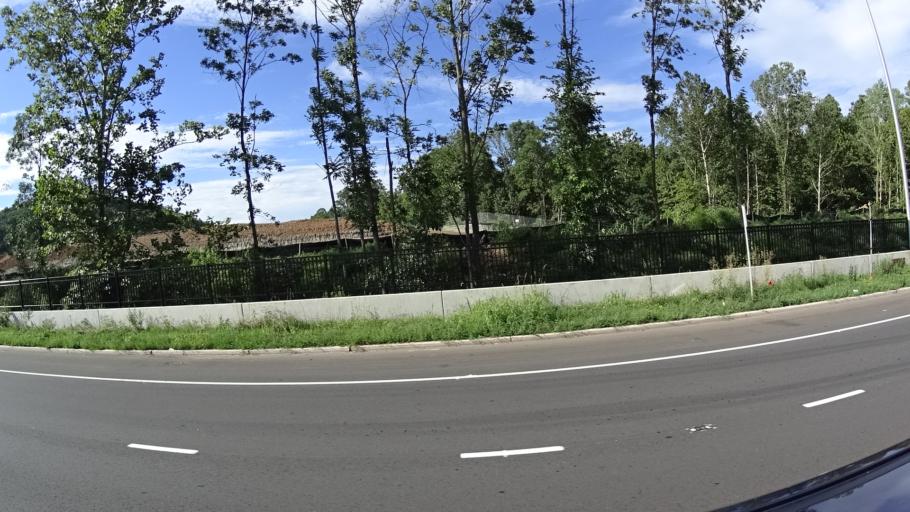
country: US
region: New Jersey
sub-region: Somerset County
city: Bound Brook
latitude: 40.5750
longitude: -74.5564
